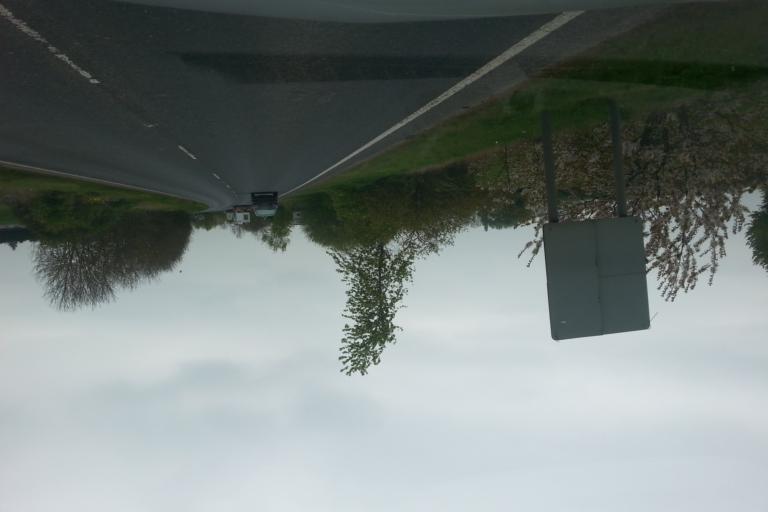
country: GB
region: England
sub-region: Cambridgeshire
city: Littleport
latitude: 52.4589
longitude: 0.2837
